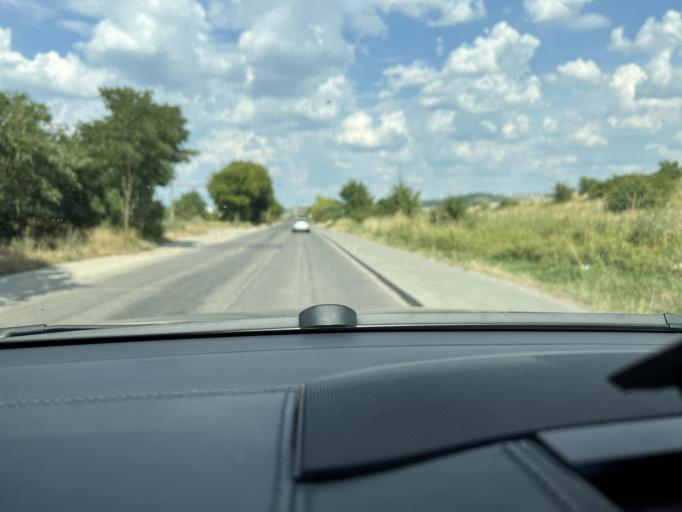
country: RO
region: Cluj
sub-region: Comuna Apahida
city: Dezmir
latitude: 46.7792
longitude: 23.6771
